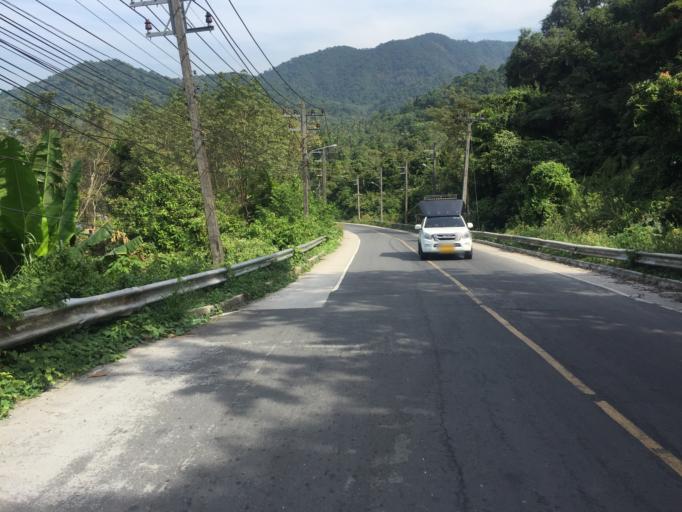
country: TH
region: Trat
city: Laem Ngop
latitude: 12.1258
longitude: 102.2701
